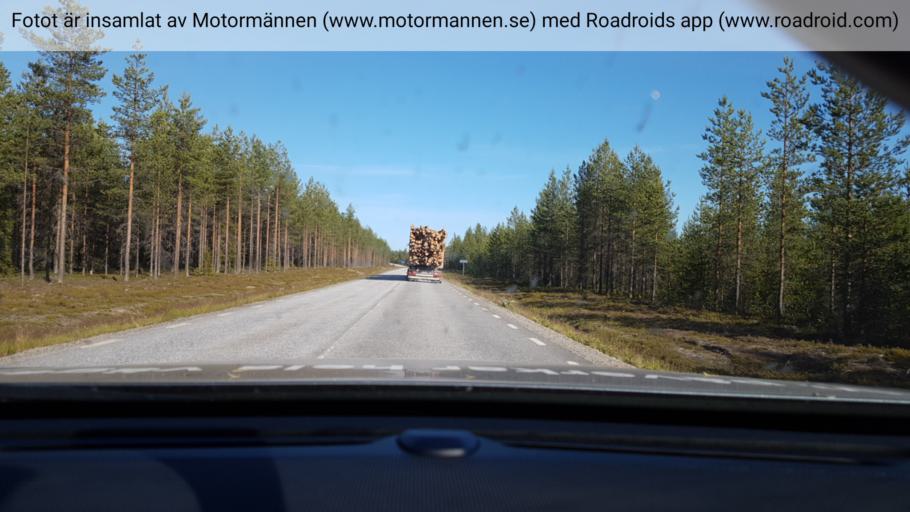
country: SE
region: Vaesterbotten
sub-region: Vindelns Kommun
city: Vindeln
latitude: 64.2088
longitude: 19.4111
